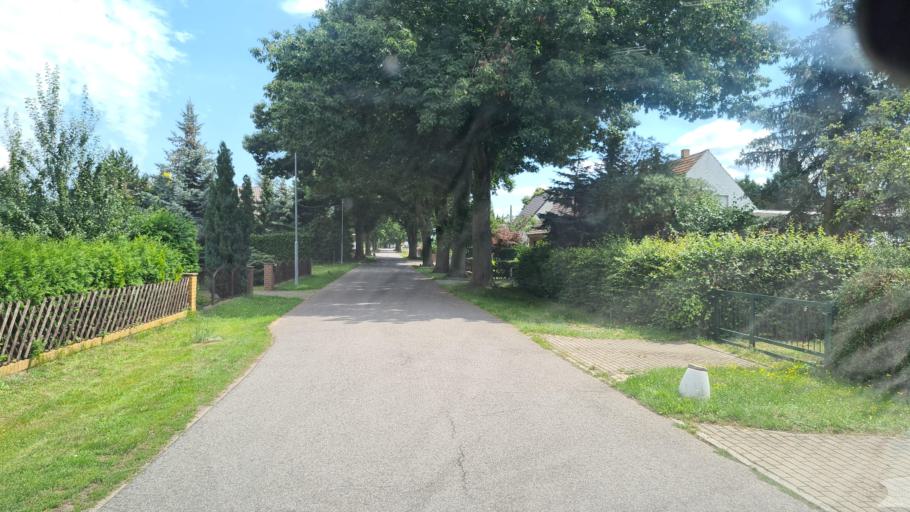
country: DE
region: Brandenburg
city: Welzow
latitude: 51.5204
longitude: 14.1745
